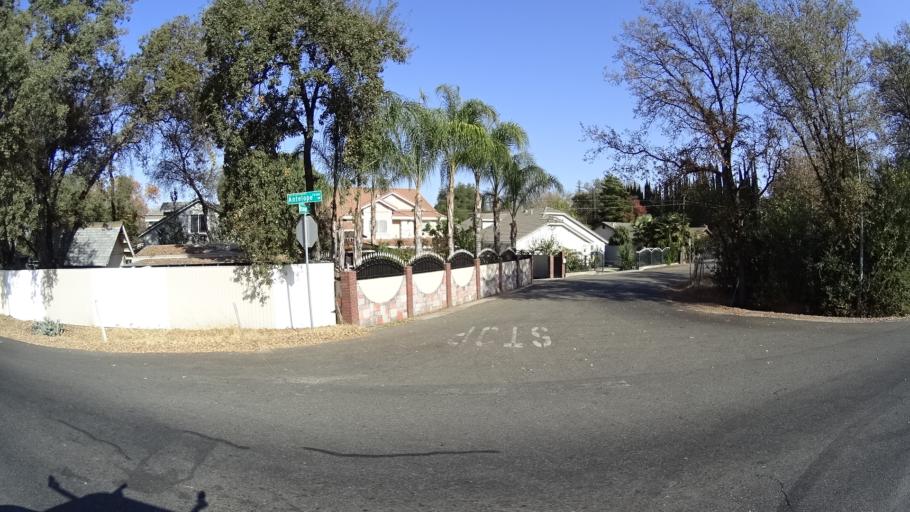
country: US
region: California
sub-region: Sacramento County
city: Citrus Heights
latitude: 38.7063
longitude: -121.2885
